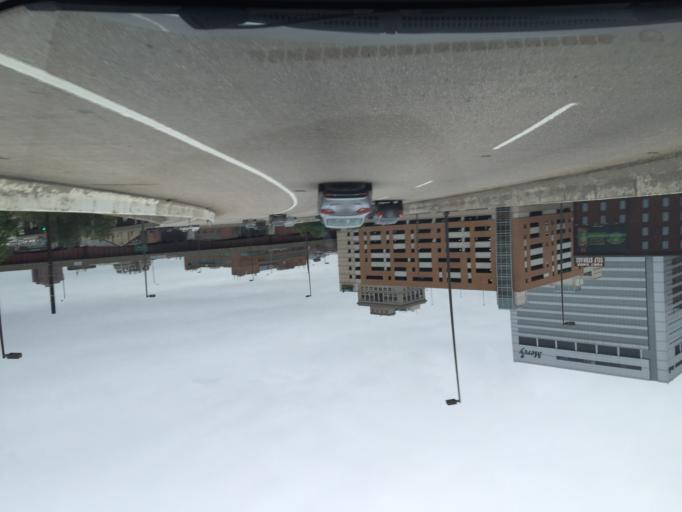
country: US
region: Maryland
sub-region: City of Baltimore
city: Baltimore
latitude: 39.2930
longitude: -76.6095
